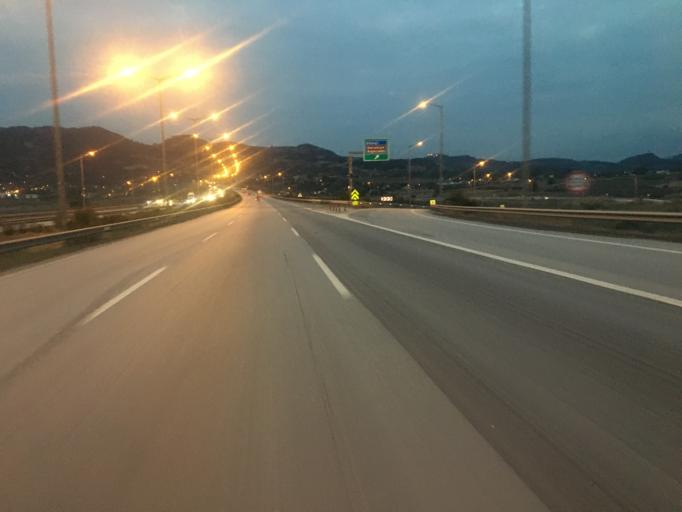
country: TR
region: Osmaniye
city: Haruniye
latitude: 37.1963
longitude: 36.4141
